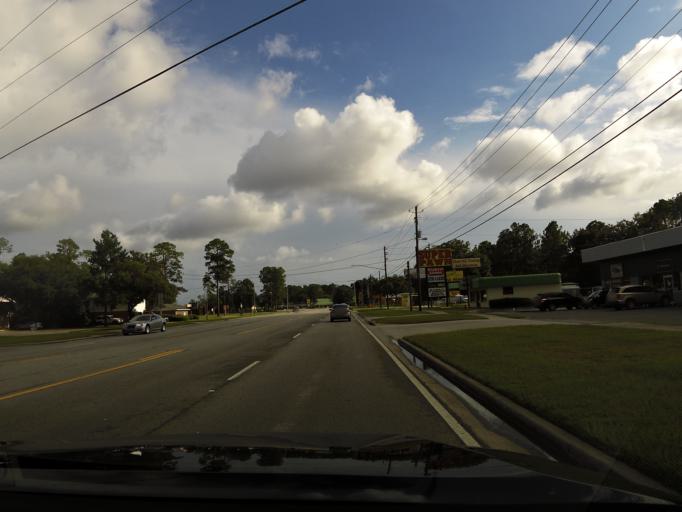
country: US
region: Georgia
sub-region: Liberty County
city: Hinesville
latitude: 31.8516
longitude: -81.6062
